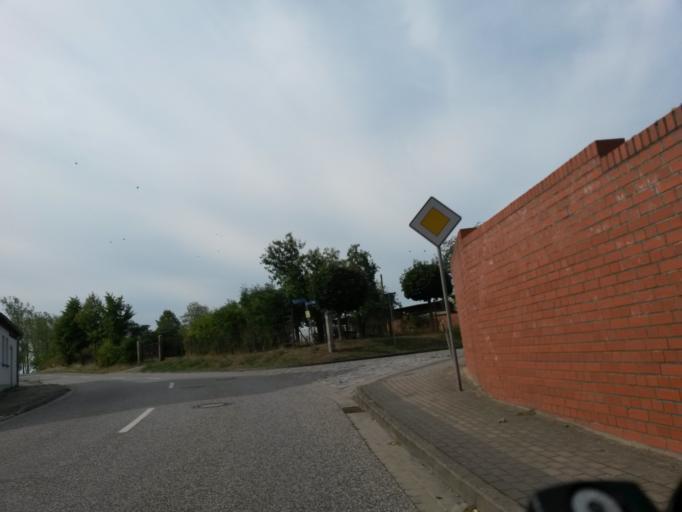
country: DE
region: Saxony-Anhalt
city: Stendal
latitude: 52.5408
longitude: 11.8857
